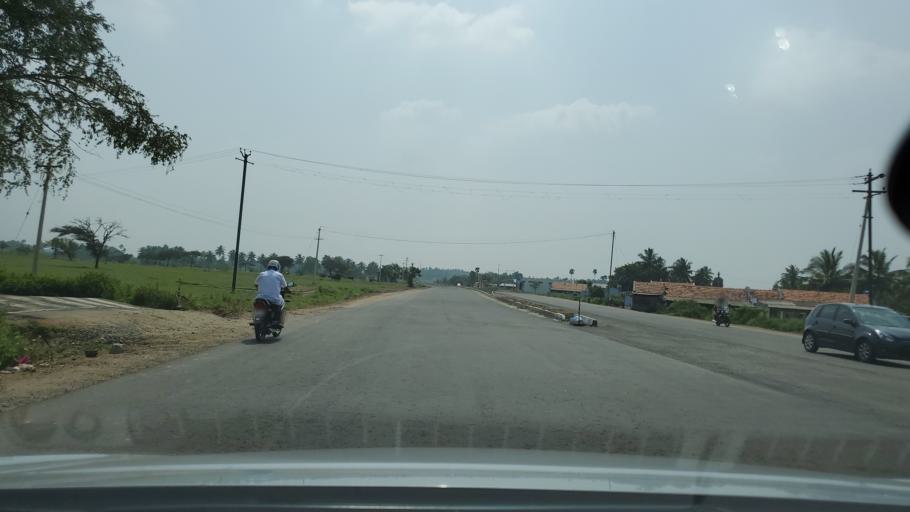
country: IN
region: Tamil Nadu
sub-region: Tiruppur
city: Kangayam
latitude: 10.9617
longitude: 77.4282
